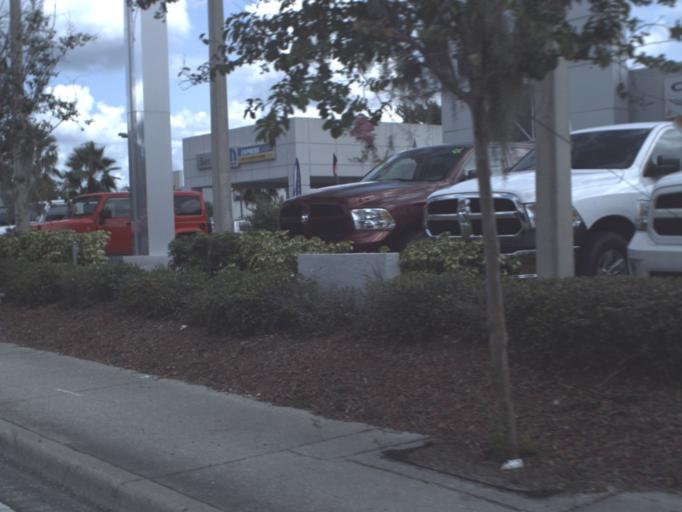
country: US
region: Florida
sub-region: Hillsborough County
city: Lake Magdalene
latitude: 28.0477
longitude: -82.4593
